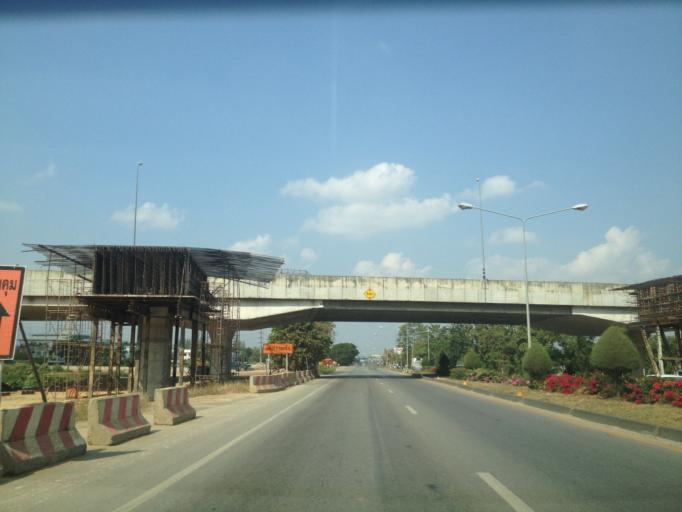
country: TH
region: Chiang Mai
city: Saraphi
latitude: 18.7350
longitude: 99.0375
